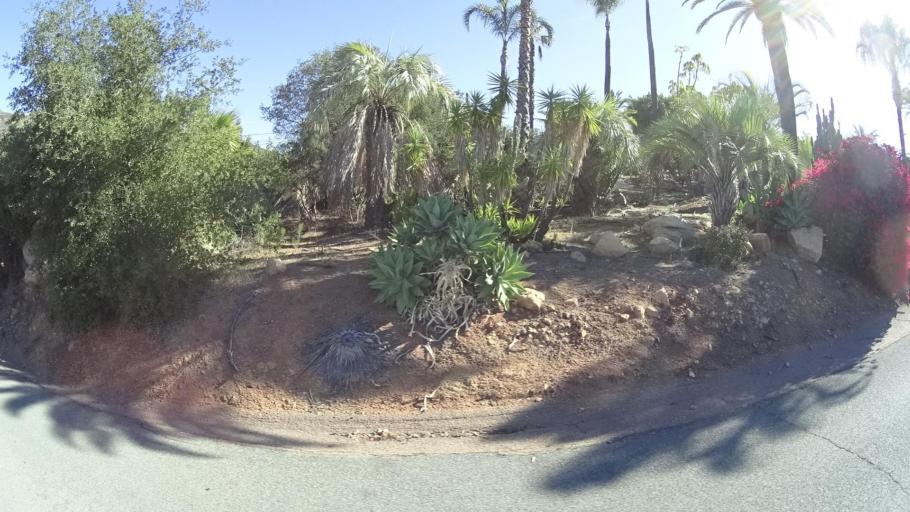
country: US
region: California
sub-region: San Diego County
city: Jamul
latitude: 32.7295
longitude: -116.8368
